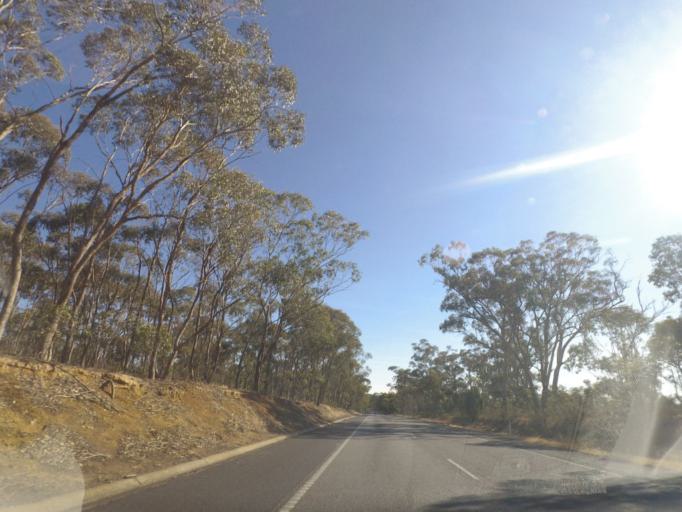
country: AU
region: Victoria
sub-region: Murrindindi
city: Kinglake West
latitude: -37.1749
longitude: 145.0732
